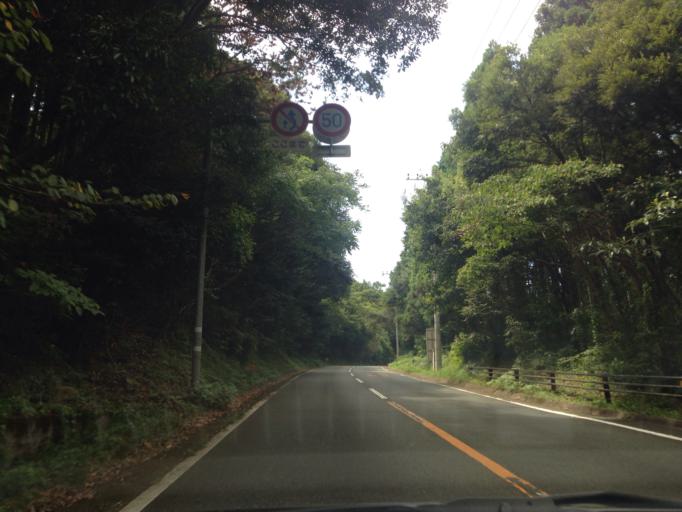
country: JP
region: Shizuoka
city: Shimoda
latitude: 34.6862
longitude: 138.7762
